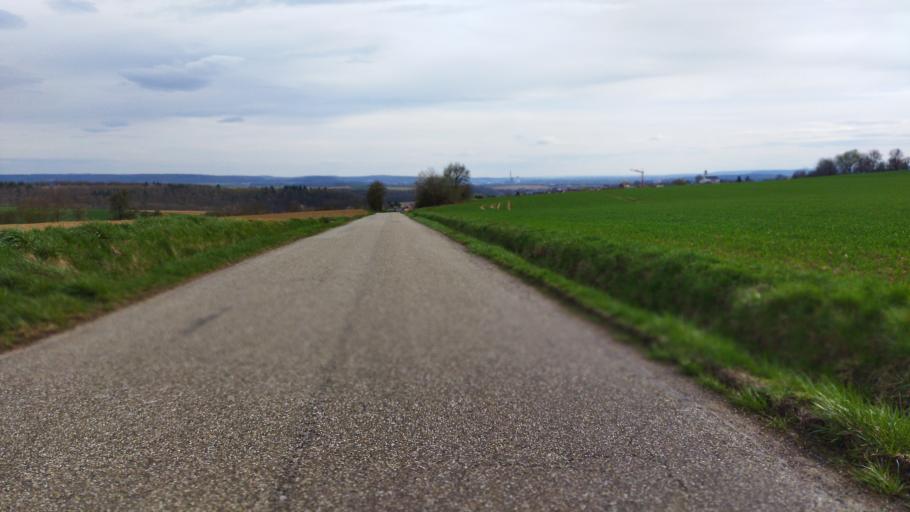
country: DE
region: Baden-Wuerttemberg
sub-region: Regierungsbezirk Stuttgart
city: Neudenau
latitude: 49.2954
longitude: 9.2274
